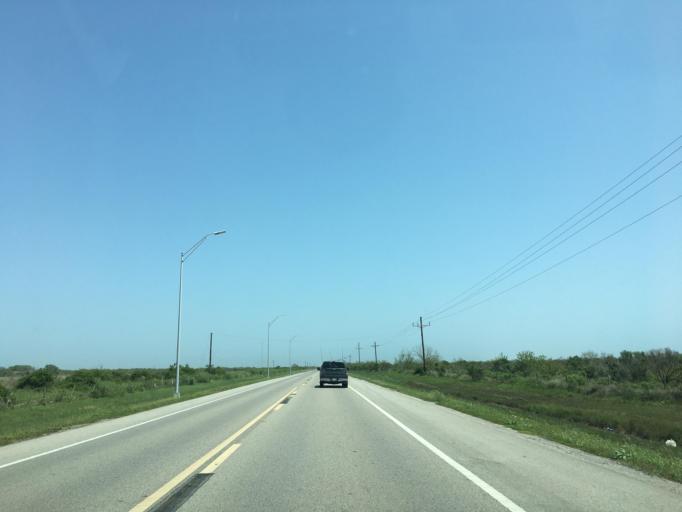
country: US
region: Texas
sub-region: Galveston County
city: Galveston
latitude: 29.3994
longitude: -94.7264
